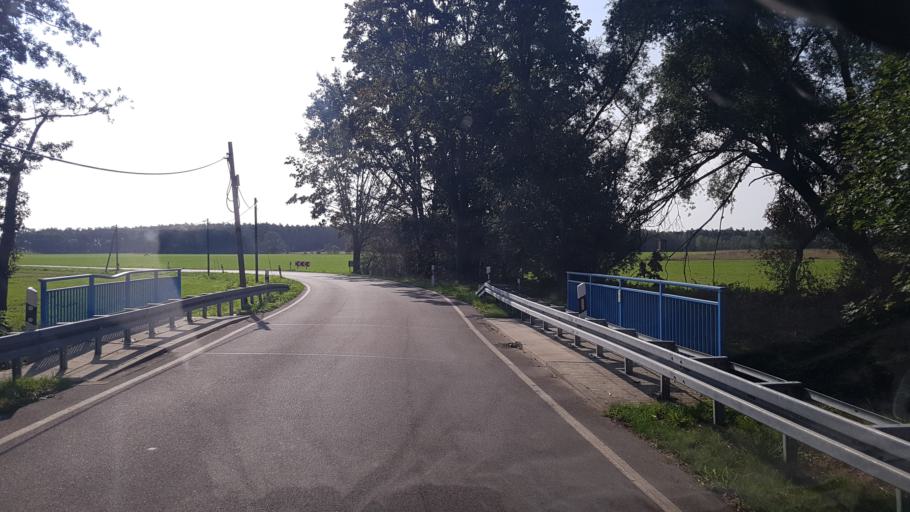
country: DE
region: Brandenburg
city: Luebben
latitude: 51.8691
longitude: 13.8640
